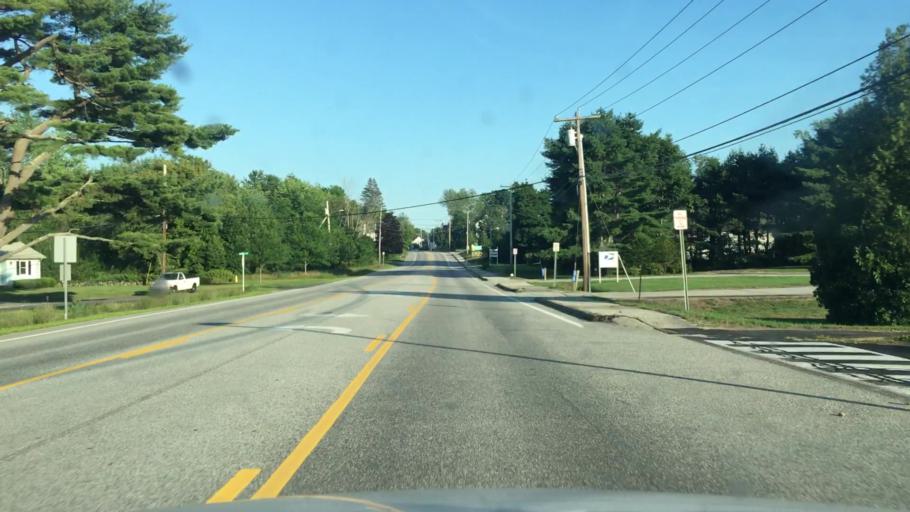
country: US
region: Maine
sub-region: Androscoggin County
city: Lisbon
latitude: 44.0234
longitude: -70.0985
